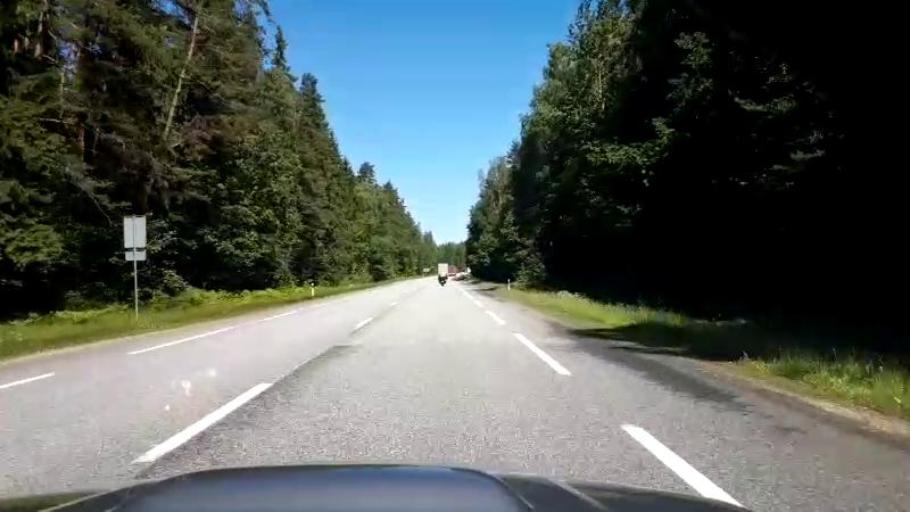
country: LV
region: Saulkrastu
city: Saulkrasti
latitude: 57.3975
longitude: 24.4282
